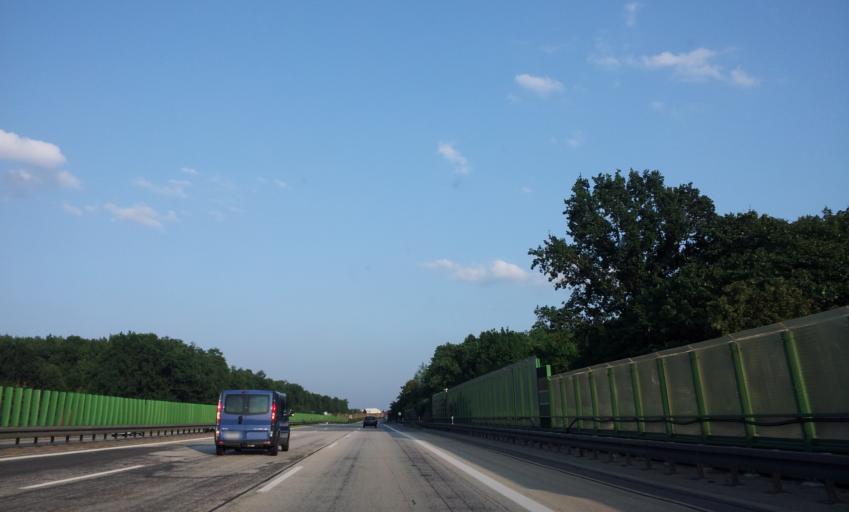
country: DE
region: Brandenburg
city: Woltersdorf
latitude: 52.4673
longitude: 13.7827
